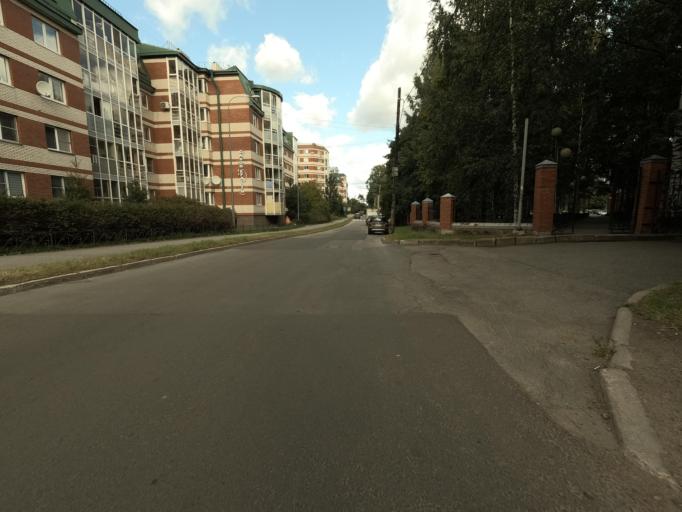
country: RU
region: St.-Petersburg
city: Krasnogvargeisky
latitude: 59.9644
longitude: 30.4893
